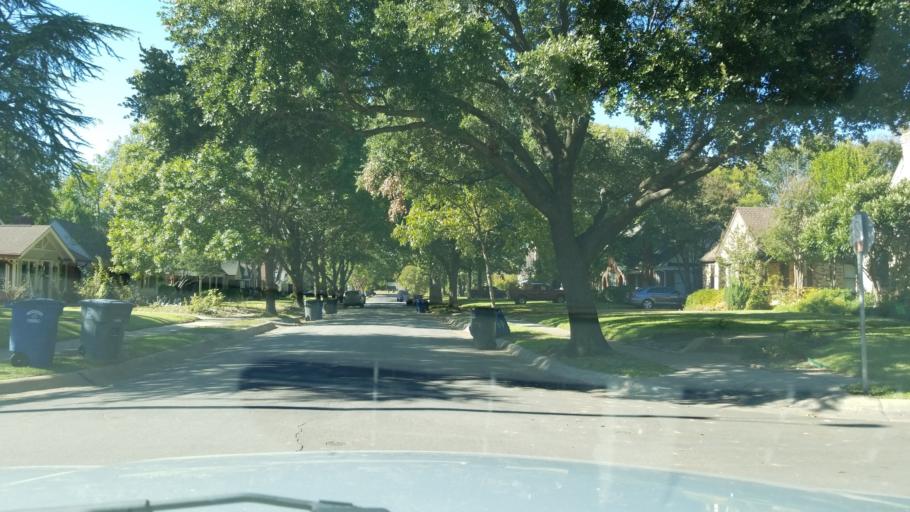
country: US
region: Texas
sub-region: Dallas County
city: Highland Park
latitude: 32.8046
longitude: -96.7445
